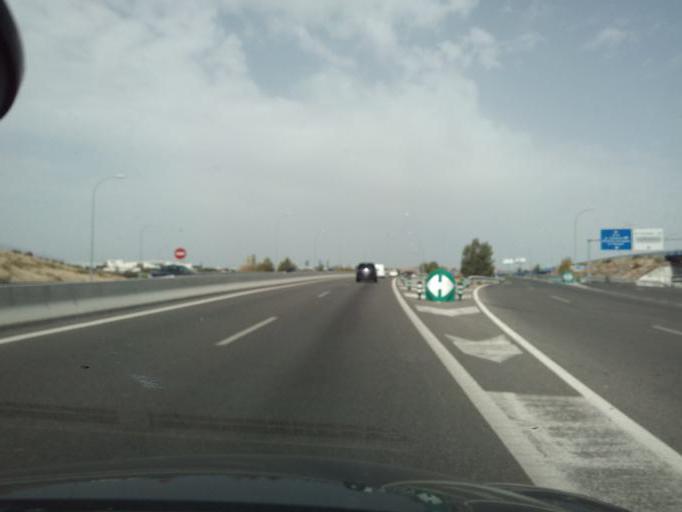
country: ES
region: Madrid
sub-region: Provincia de Madrid
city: Barajas de Madrid
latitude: 40.4694
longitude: -3.5983
